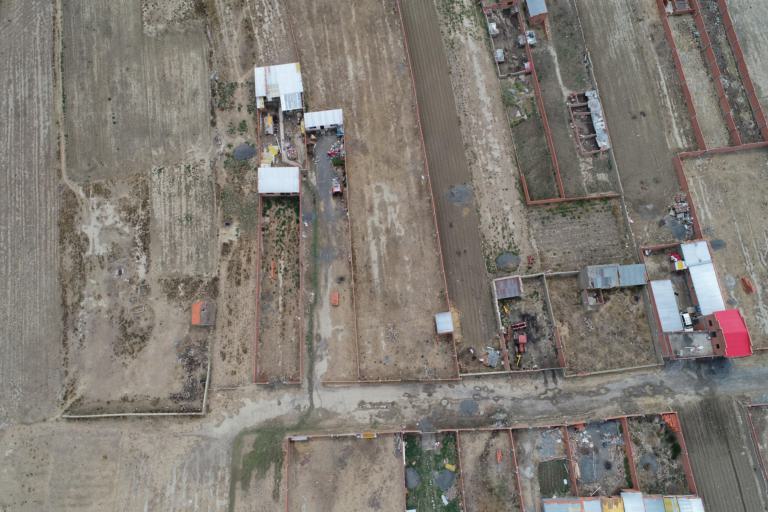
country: BO
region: La Paz
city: Achacachi
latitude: -16.0531
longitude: -68.6844
